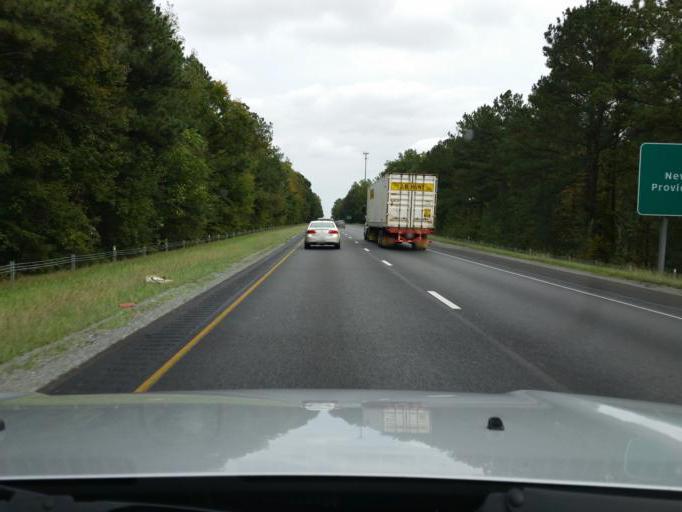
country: US
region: Virginia
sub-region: New Kent County
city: New Kent
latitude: 37.4961
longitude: -77.0315
